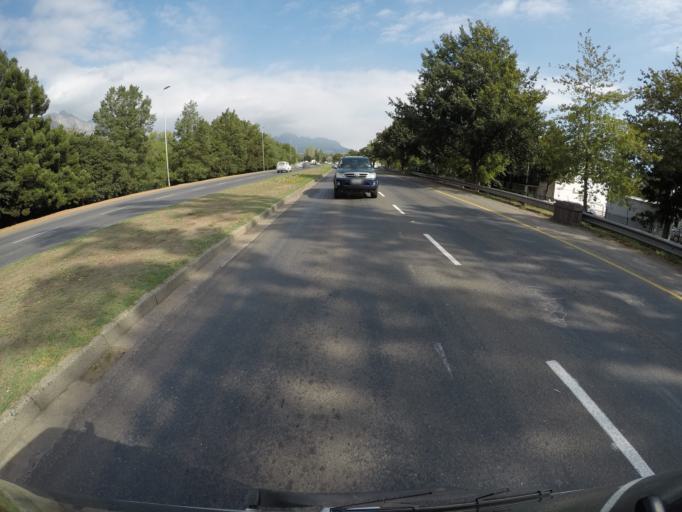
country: ZA
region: Western Cape
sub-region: Cape Winelands District Municipality
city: Stellenbosch
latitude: -33.9419
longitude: 18.8520
